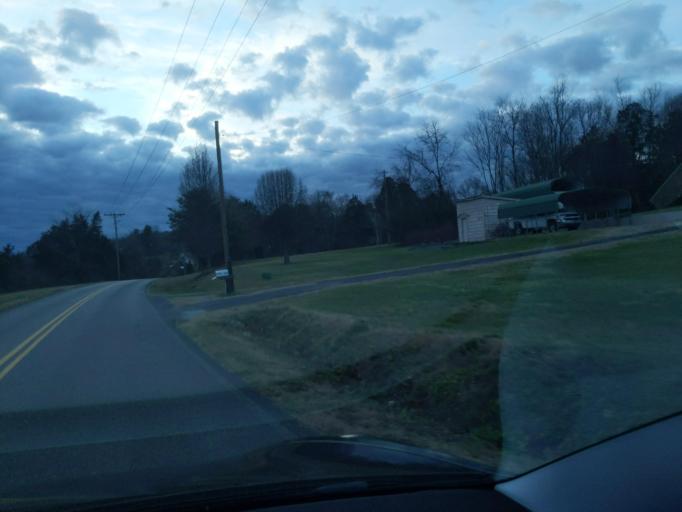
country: US
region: Tennessee
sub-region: Jefferson County
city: White Pine
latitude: 36.1077
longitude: -83.3503
